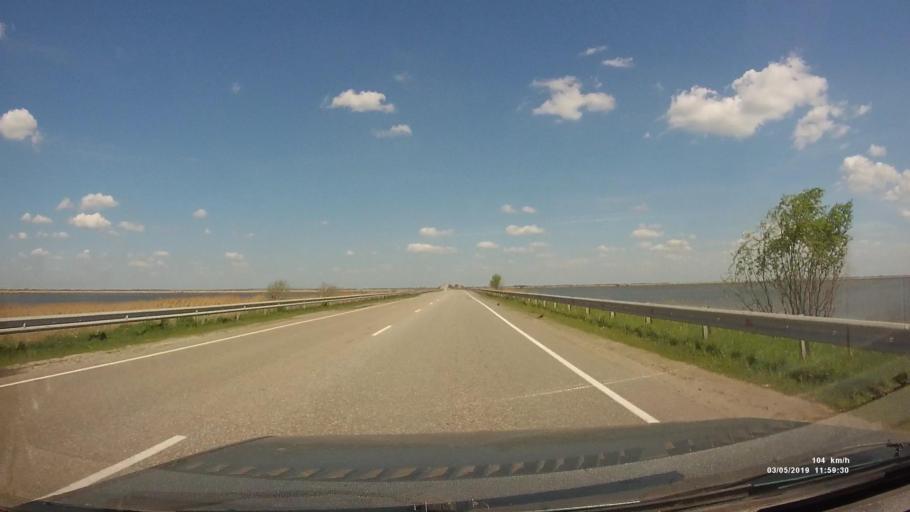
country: RU
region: Rostov
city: Bagayevskaya
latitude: 47.2358
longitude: 40.3310
